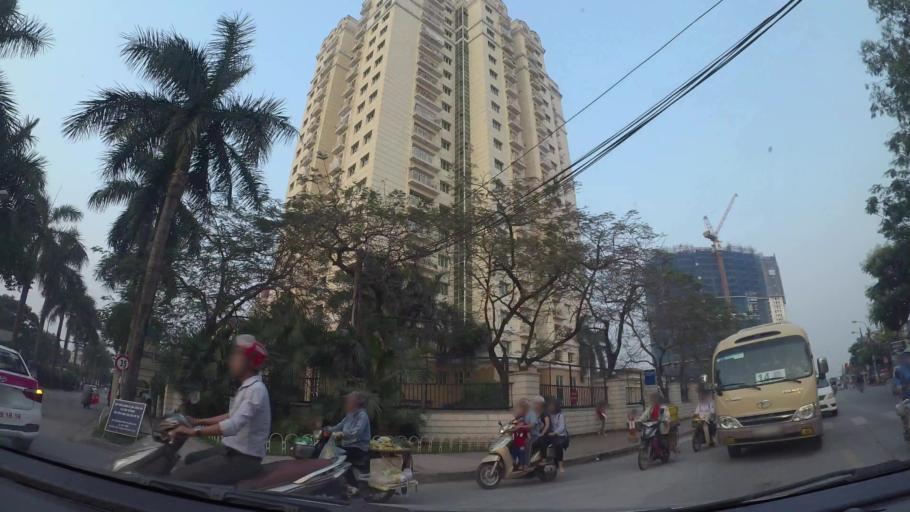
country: VN
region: Ha Noi
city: Tay Ho
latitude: 21.0710
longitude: 105.8077
